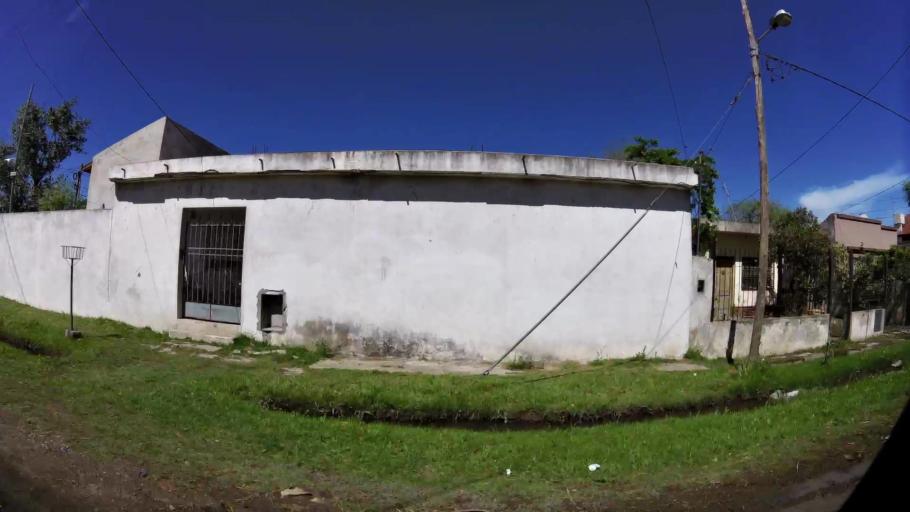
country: AR
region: Buenos Aires
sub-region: Partido de Quilmes
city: Quilmes
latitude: -34.7004
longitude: -58.2789
